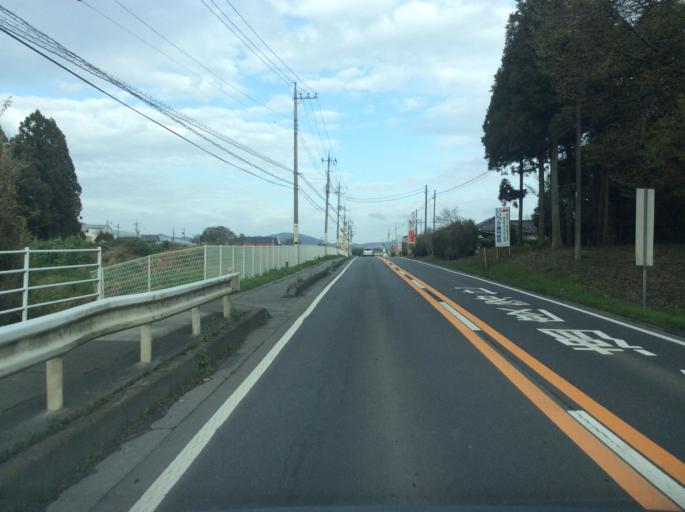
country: JP
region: Ibaraki
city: Tsukuba
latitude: 36.1799
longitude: 140.0467
